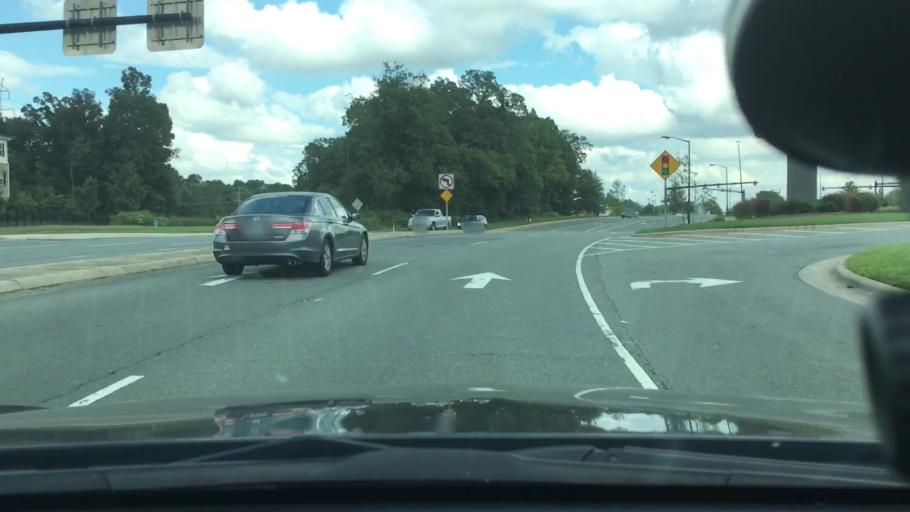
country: US
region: North Carolina
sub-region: Alamance County
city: Elon
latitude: 36.0689
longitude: -79.5184
